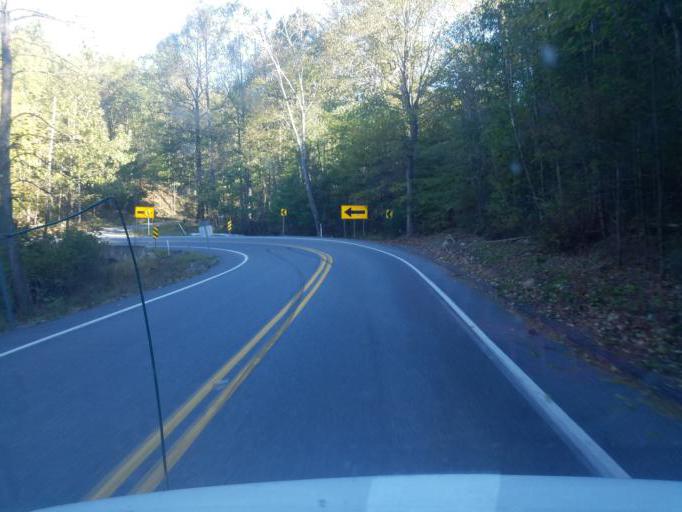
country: US
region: Pennsylvania
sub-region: Franklin County
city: Mont Alto
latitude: 39.8525
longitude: -77.5174
